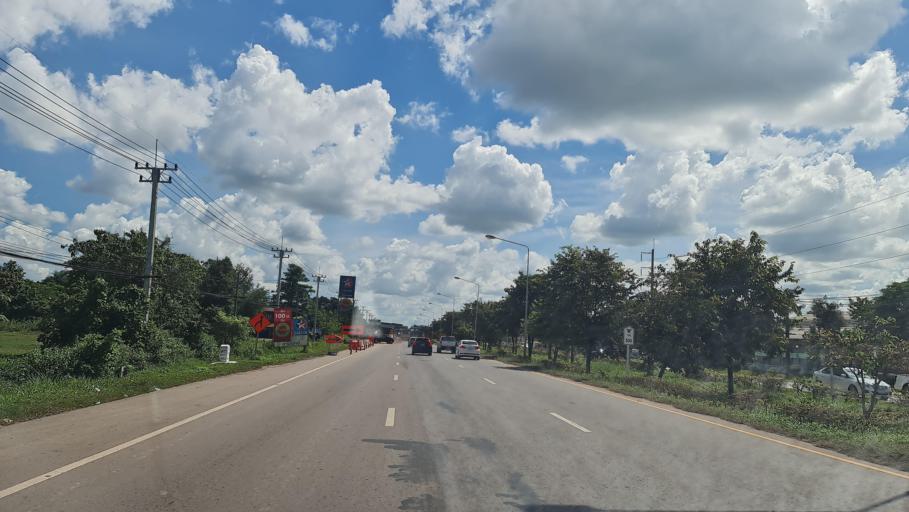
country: TH
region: Nong Khai
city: Nong Khai
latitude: 17.8042
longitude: 102.7610
